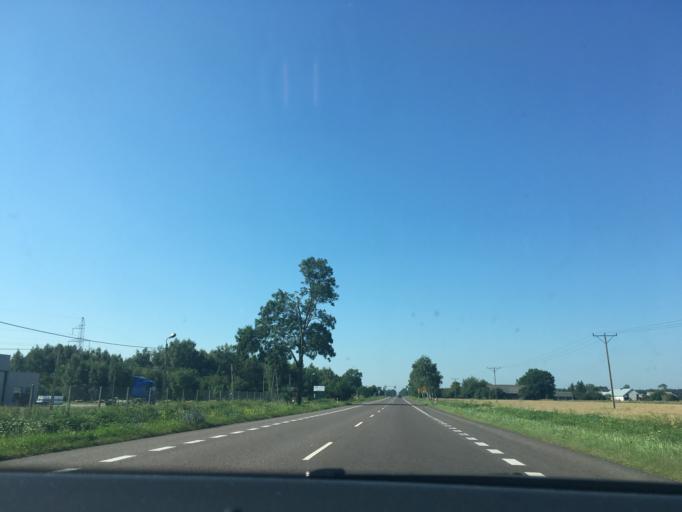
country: PL
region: Lublin Voivodeship
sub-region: Powiat radzynski
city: Radzyn Podlaski
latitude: 51.7752
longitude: 22.5880
